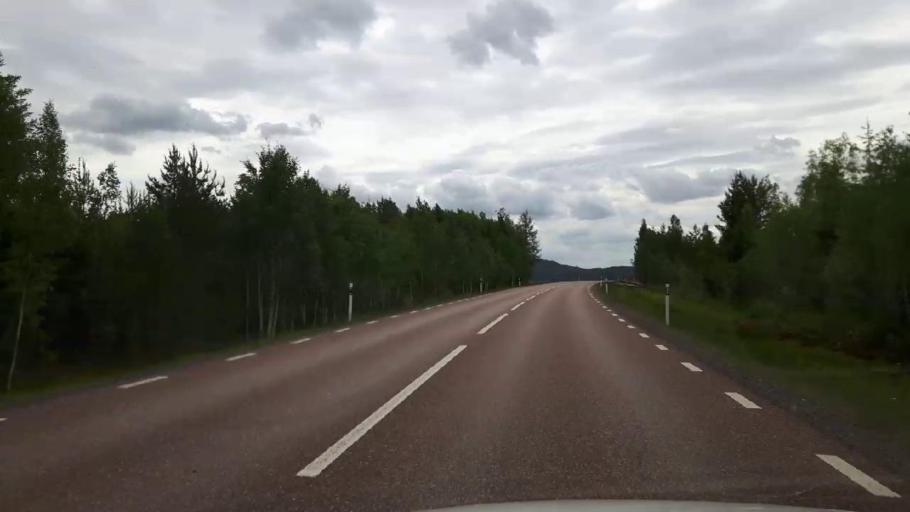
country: SE
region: Dalarna
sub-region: Hedemora Kommun
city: Brunna
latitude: 60.2488
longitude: 16.0106
